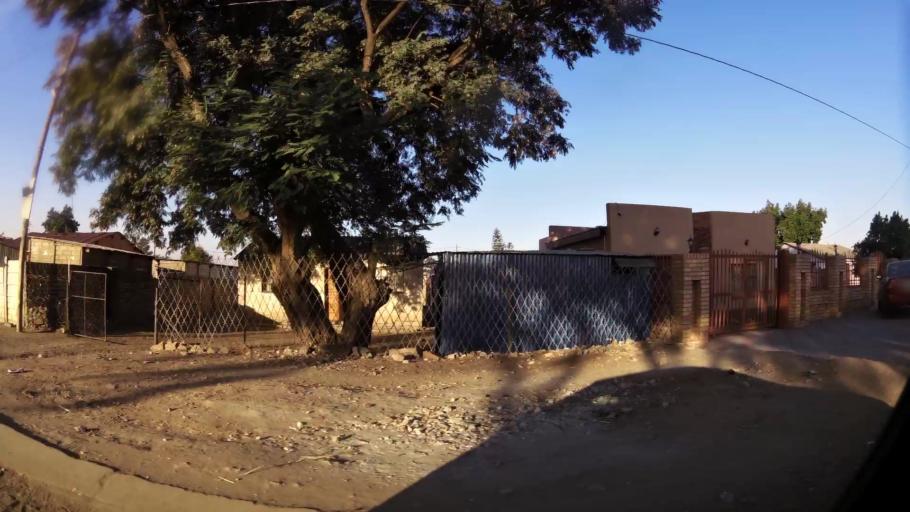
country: ZA
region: North-West
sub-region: Bojanala Platinum District Municipality
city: Rustenburg
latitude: -25.6296
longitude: 27.2155
